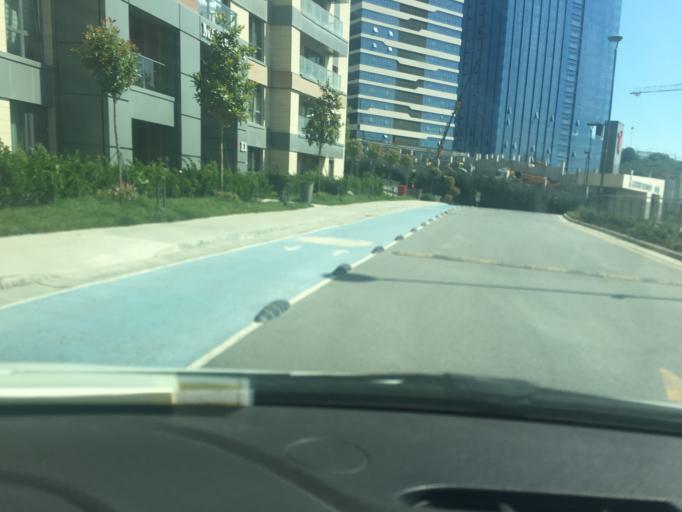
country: TR
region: Istanbul
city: Sisli
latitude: 41.0910
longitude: 28.9501
